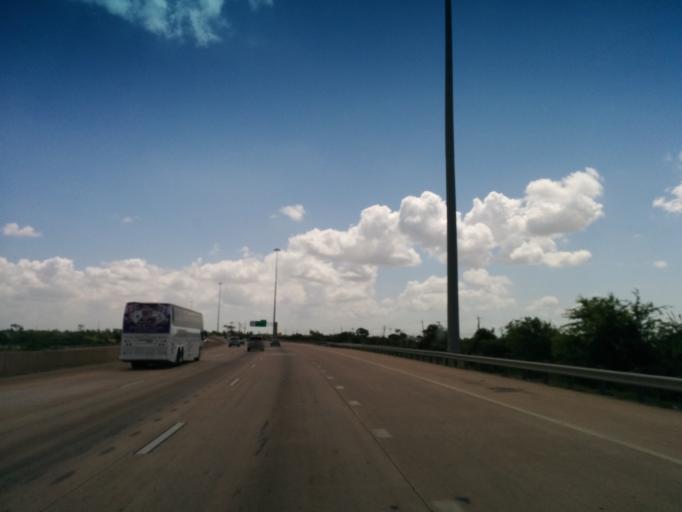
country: US
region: Texas
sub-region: Harris County
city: Channelview
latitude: 29.7908
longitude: -95.0854
